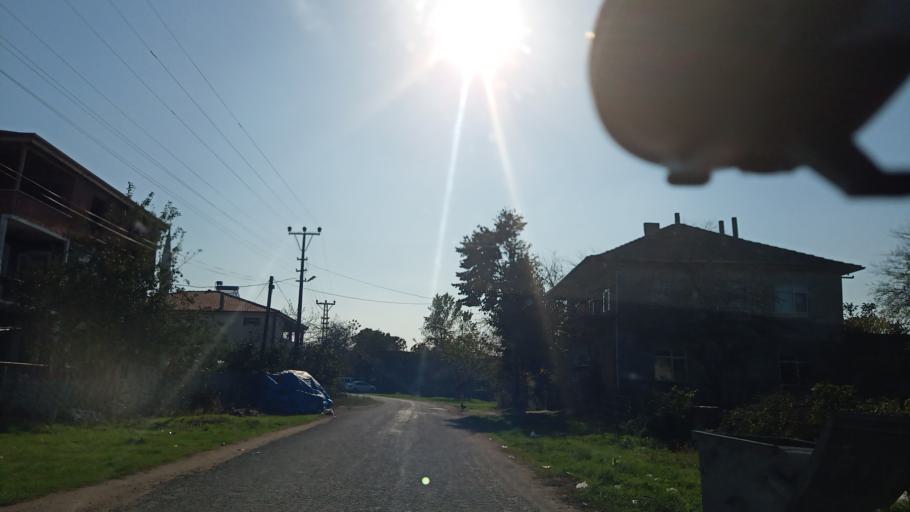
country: TR
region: Sakarya
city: Karasu
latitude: 41.0719
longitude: 30.8022
